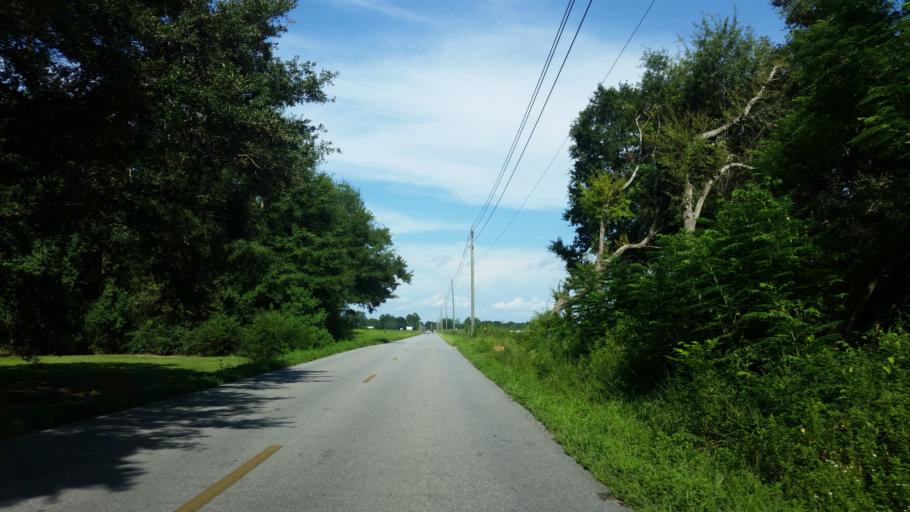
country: US
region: Florida
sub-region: Santa Rosa County
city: Pace
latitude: 30.6185
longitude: -87.1573
